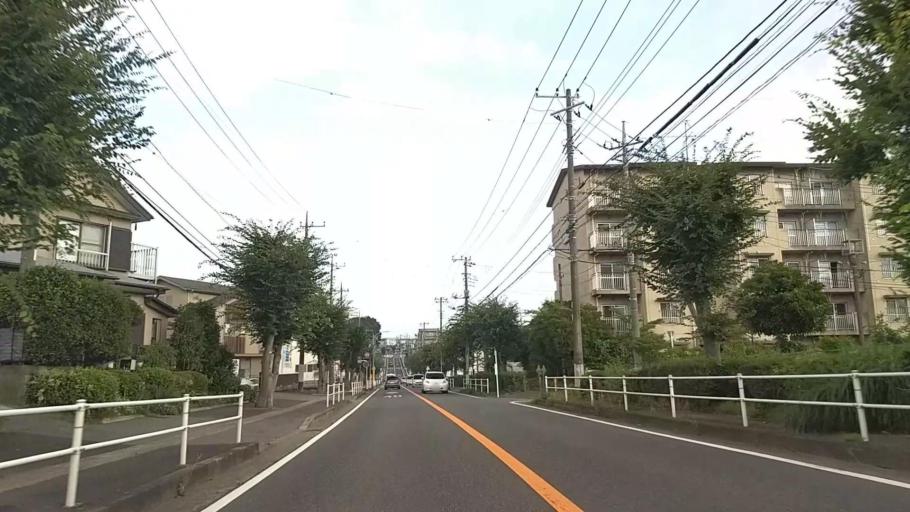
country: JP
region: Kanagawa
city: Isehara
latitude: 35.3965
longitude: 139.3004
